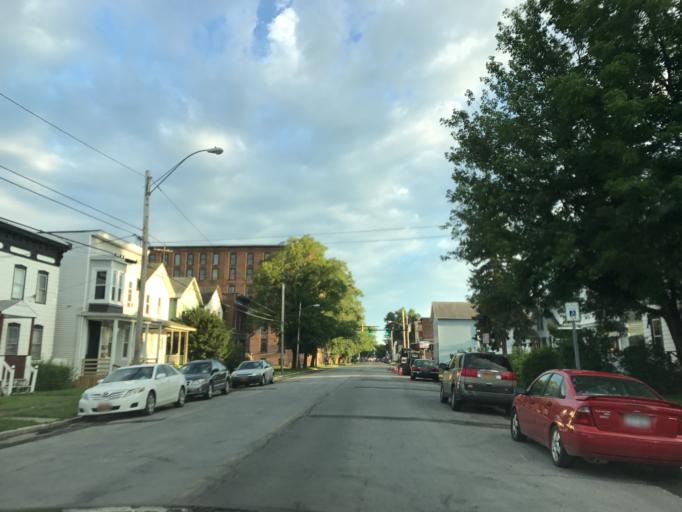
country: US
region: New York
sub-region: Saratoga County
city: Waterford
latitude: 42.7828
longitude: -73.6735
